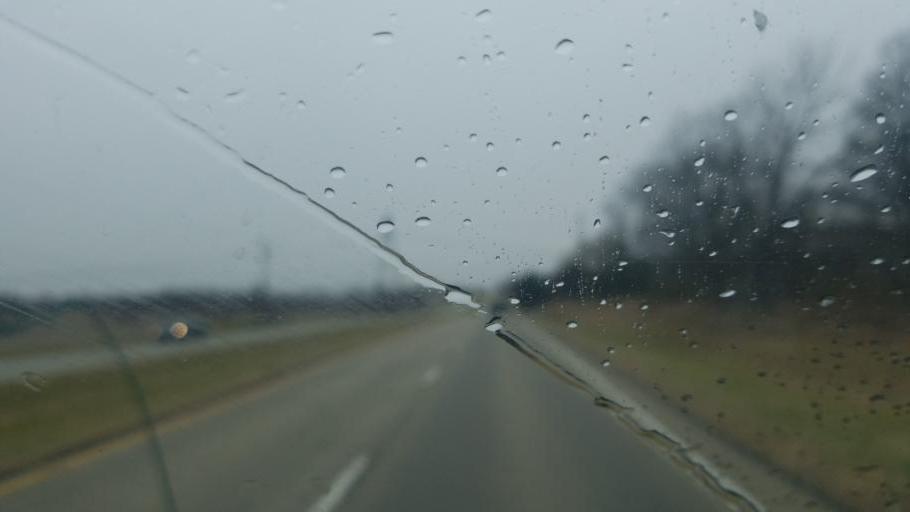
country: US
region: Indiana
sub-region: Hancock County
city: Greenfield
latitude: 39.7899
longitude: -85.6612
